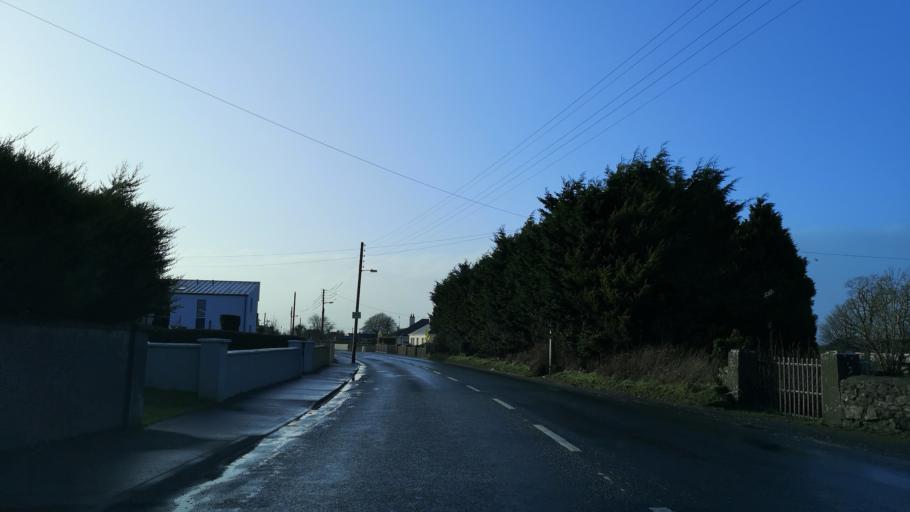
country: IE
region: Connaught
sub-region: County Galway
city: Tuam
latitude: 53.5067
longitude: -8.8321
